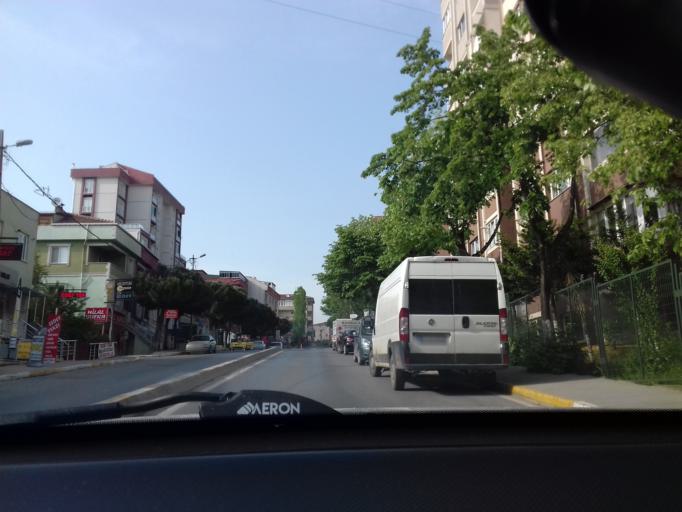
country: TR
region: Istanbul
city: Pendik
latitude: 40.9117
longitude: 29.2826
